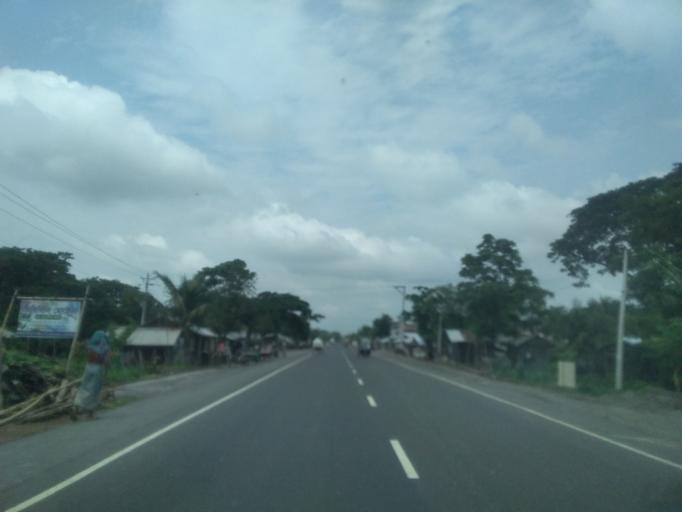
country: BD
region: Khulna
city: Kesabpur
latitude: 22.7931
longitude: 89.2228
